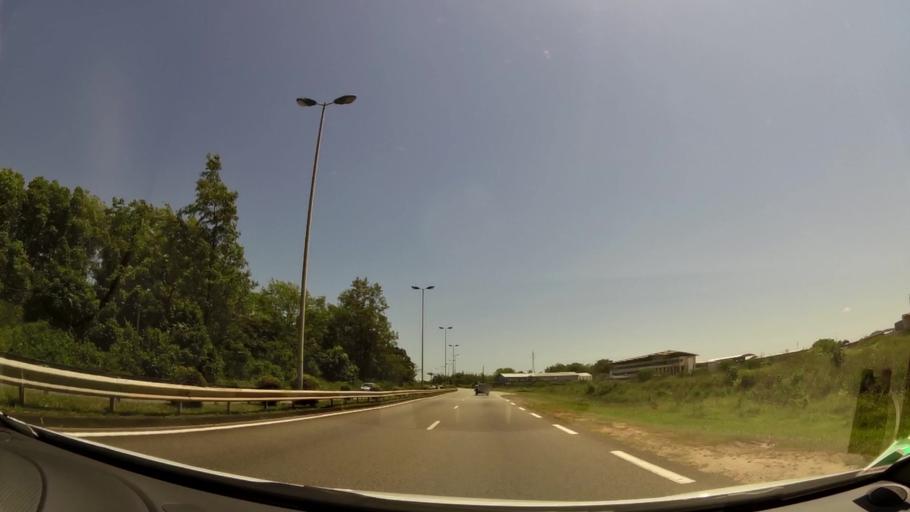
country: GF
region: Guyane
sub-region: Guyane
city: Cayenne
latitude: 4.9233
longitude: -52.3295
